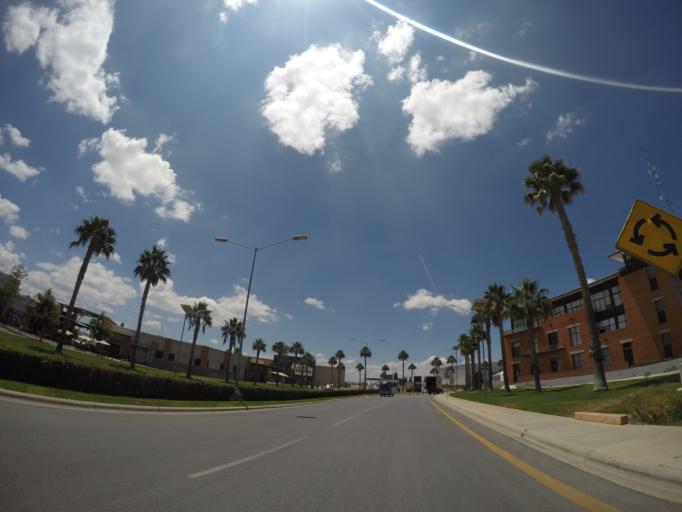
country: MX
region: San Luis Potosi
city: La Pila
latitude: 22.0419
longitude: -100.8939
